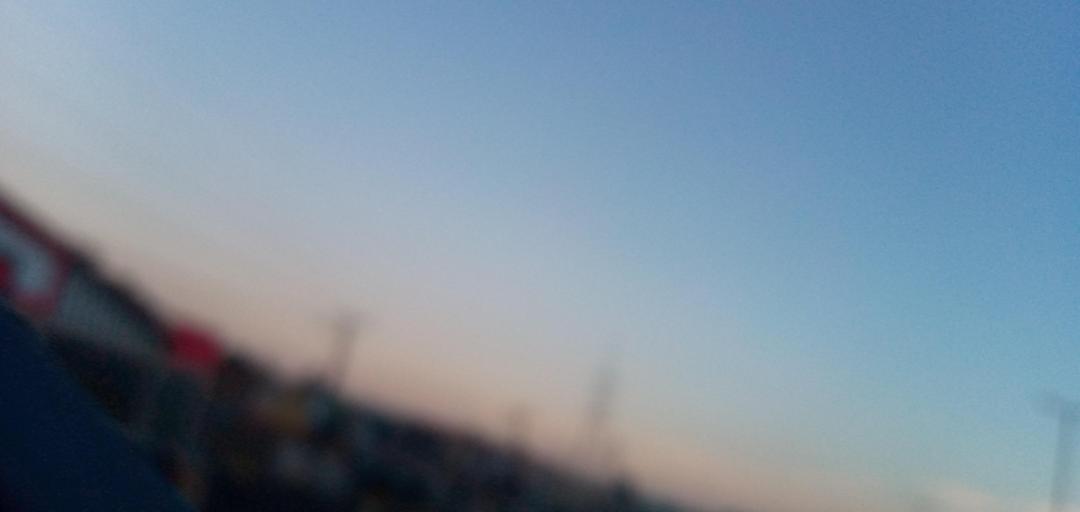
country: PK
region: Khyber Pakhtunkhwa
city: Peshawar
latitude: 34.0211
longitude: 71.6216
